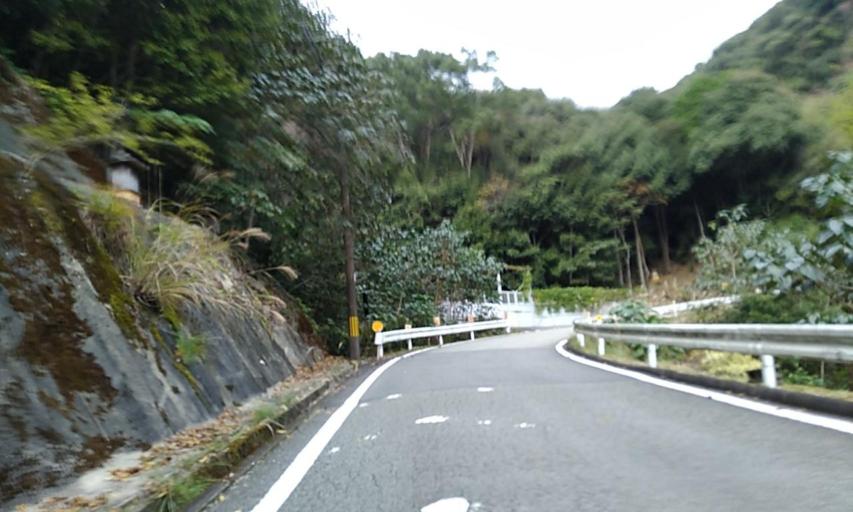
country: JP
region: Wakayama
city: Shingu
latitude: 33.5434
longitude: 135.8305
